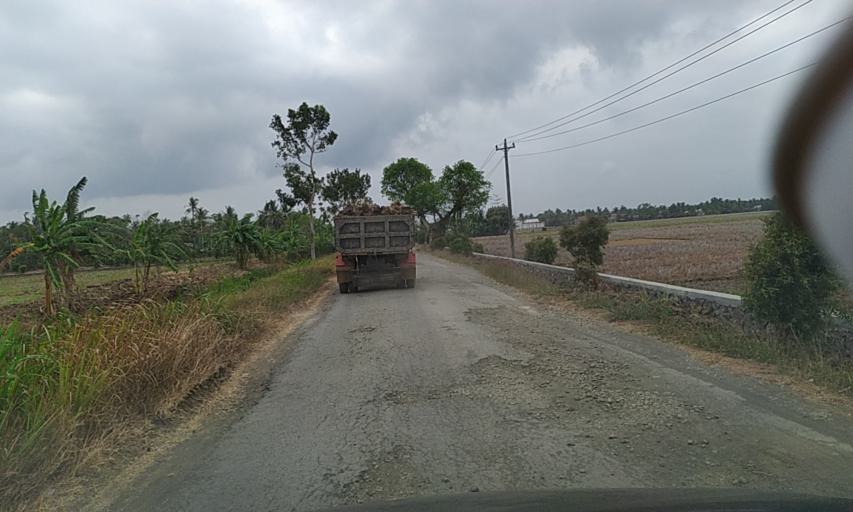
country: ID
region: Central Java
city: Jeruklegi
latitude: -7.6405
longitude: 108.9508
